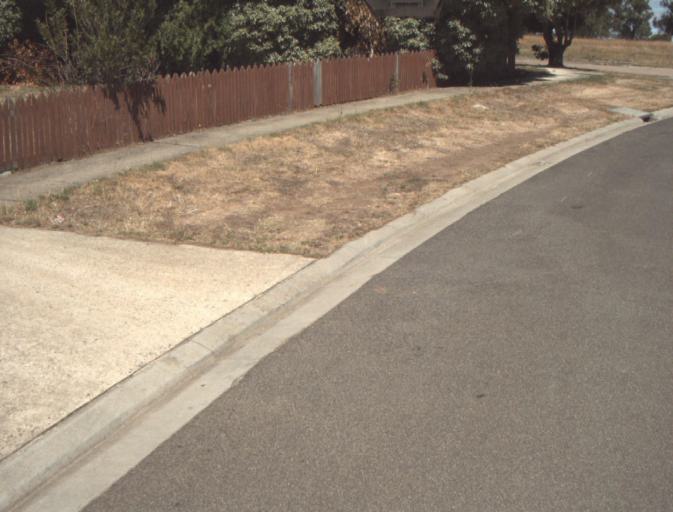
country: AU
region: Tasmania
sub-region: Launceston
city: Mayfield
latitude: -41.3754
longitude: 147.1409
